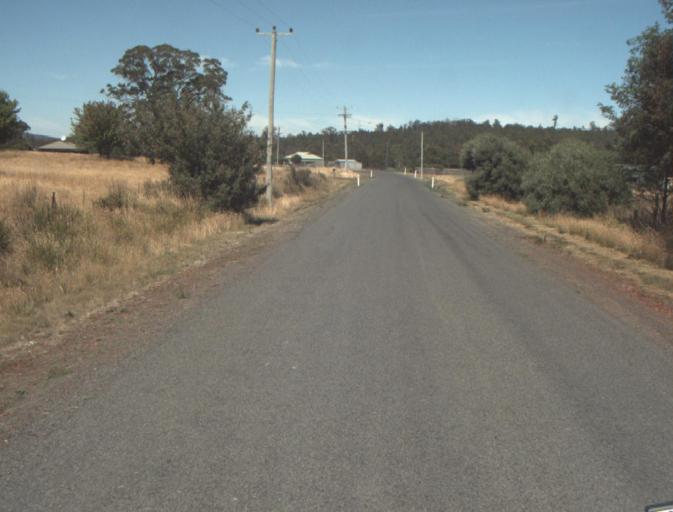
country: AU
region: Tasmania
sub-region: Launceston
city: Newstead
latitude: -41.3743
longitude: 147.2970
